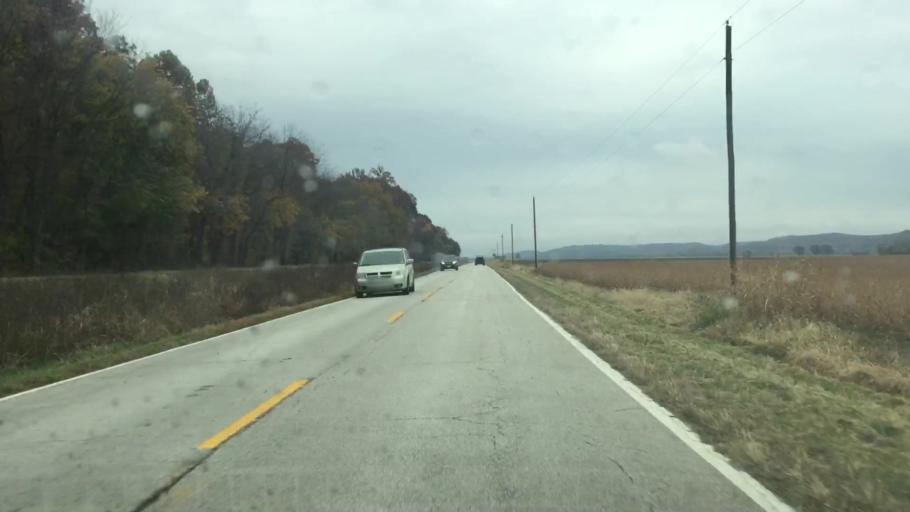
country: US
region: Missouri
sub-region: Gasconade County
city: Hermann
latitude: 38.7025
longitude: -91.5807
